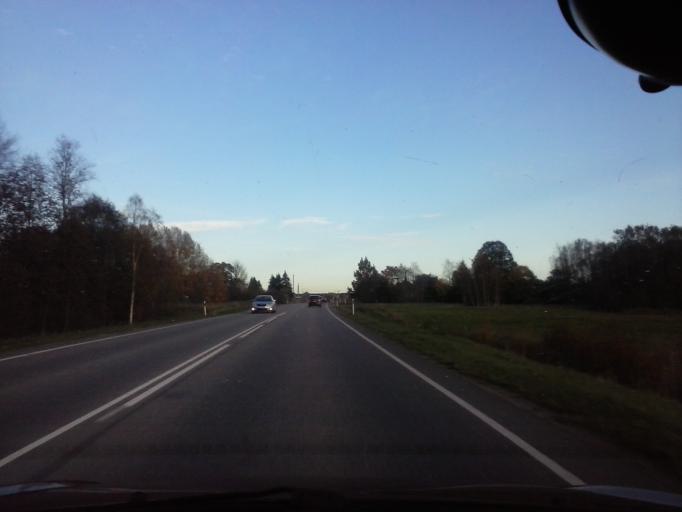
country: EE
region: Laeaene
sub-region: Ridala Parish
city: Uuemoisa
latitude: 58.9731
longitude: 23.8563
